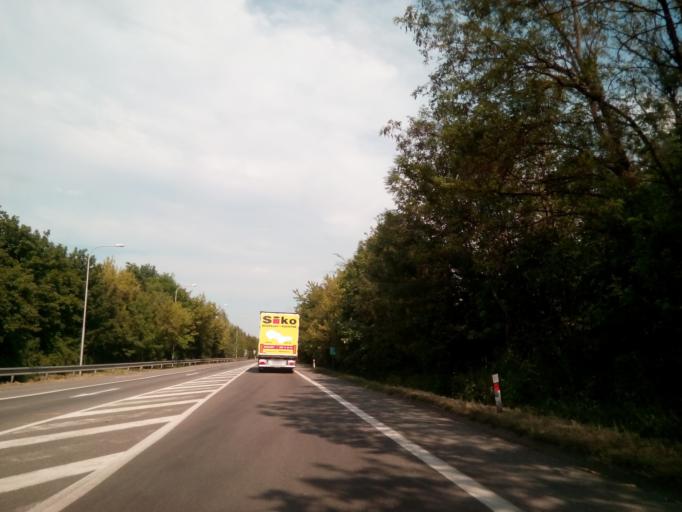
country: CZ
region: South Moravian
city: Slavkov u Brna
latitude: 49.1467
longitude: 16.8797
